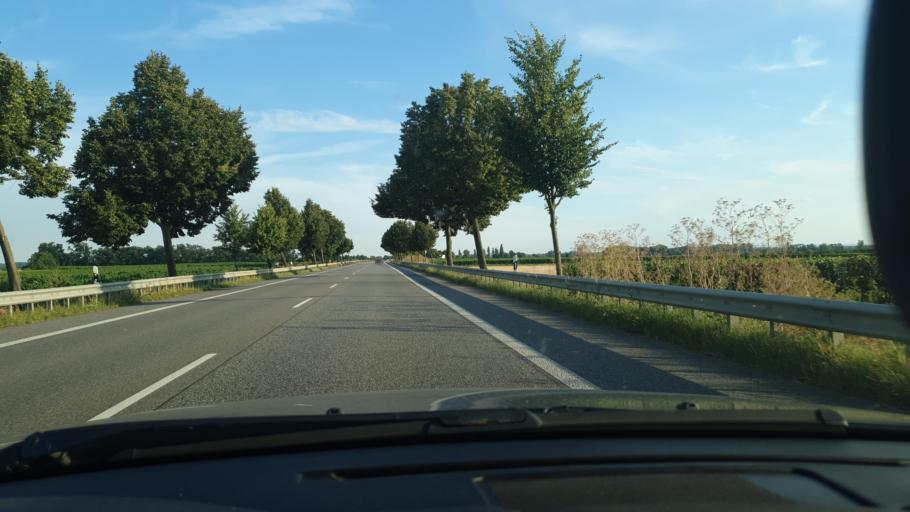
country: DE
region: Rheinland-Pfalz
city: Alsheim
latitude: 49.7461
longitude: 8.3520
